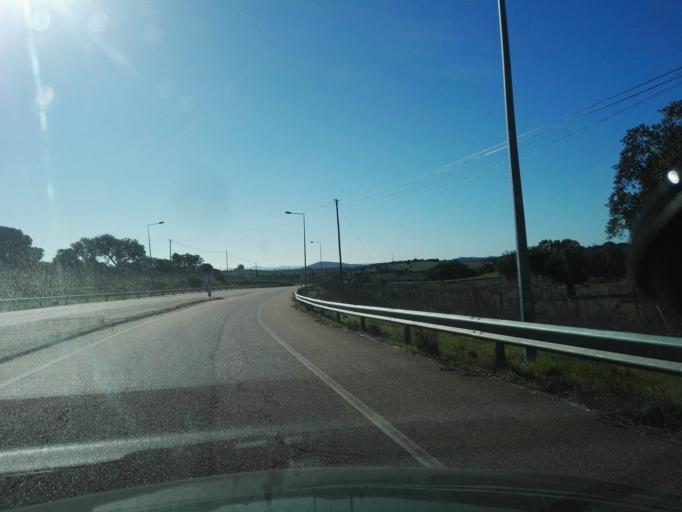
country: PT
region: Portalegre
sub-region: Elvas
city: Elvas
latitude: 38.9060
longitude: -7.1792
